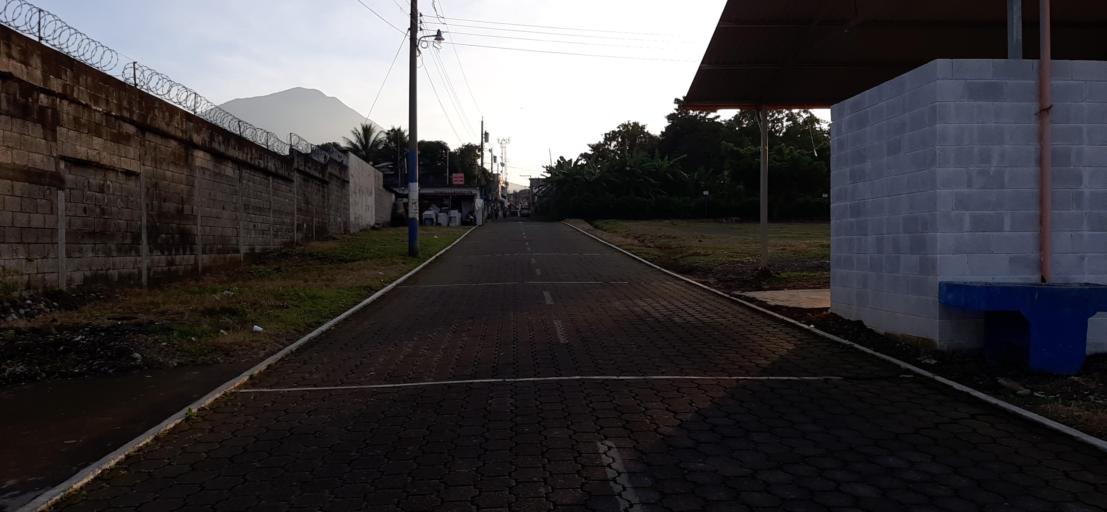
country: GT
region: Retalhuleu
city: San Felipe
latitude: 14.6228
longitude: -91.6001
